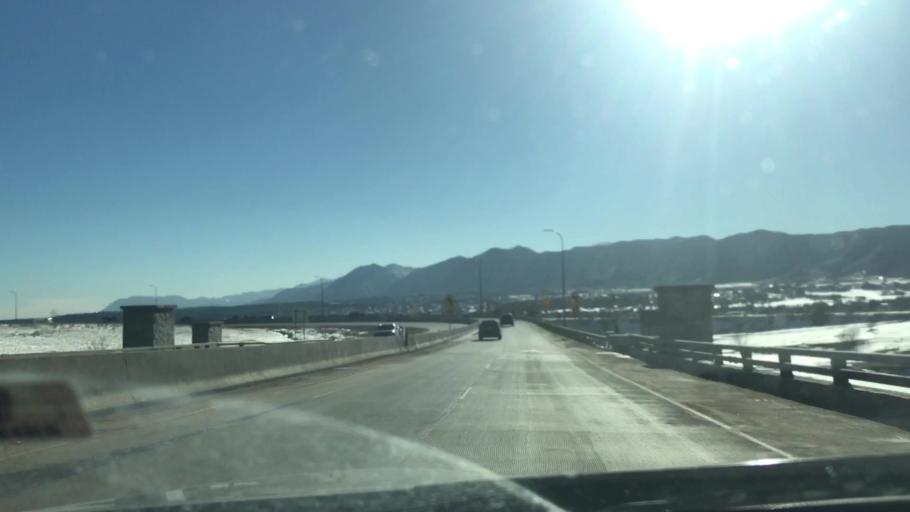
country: US
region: Colorado
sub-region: El Paso County
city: Monument
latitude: 39.0899
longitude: -104.8645
